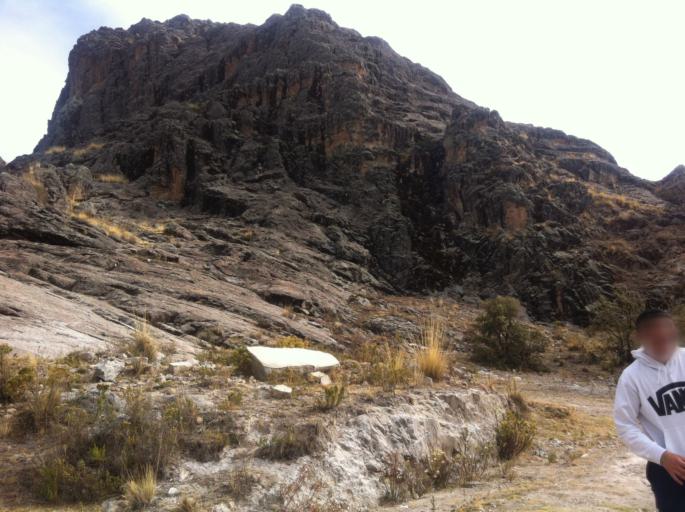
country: PE
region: Puno
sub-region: Yunguyo
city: Yunguyo
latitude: -16.1887
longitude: -69.0826
